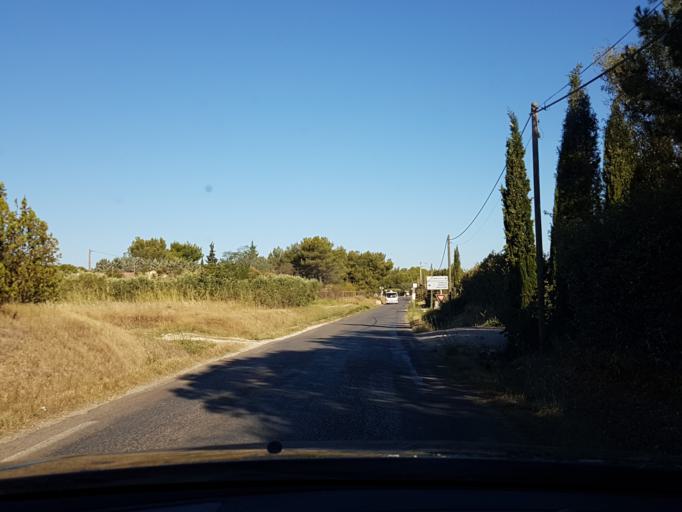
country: FR
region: Provence-Alpes-Cote d'Azur
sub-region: Departement des Bouches-du-Rhone
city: Eygalieres
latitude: 43.7652
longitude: 4.9285
